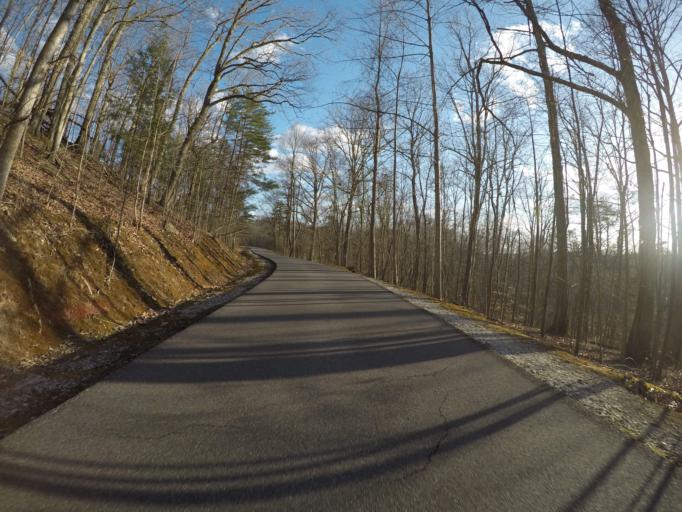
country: US
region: West Virginia
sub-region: Kanawha County
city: Charleston
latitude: 38.3902
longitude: -81.5694
